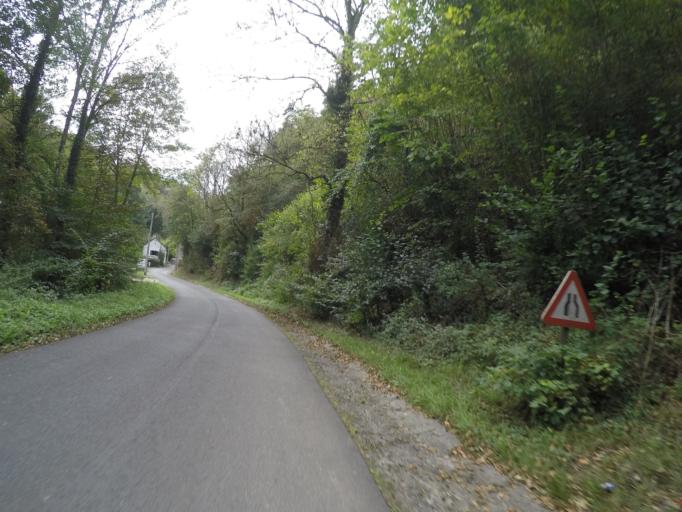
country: BE
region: Wallonia
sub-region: Province de Namur
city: Dinant
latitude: 50.2755
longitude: 4.9527
